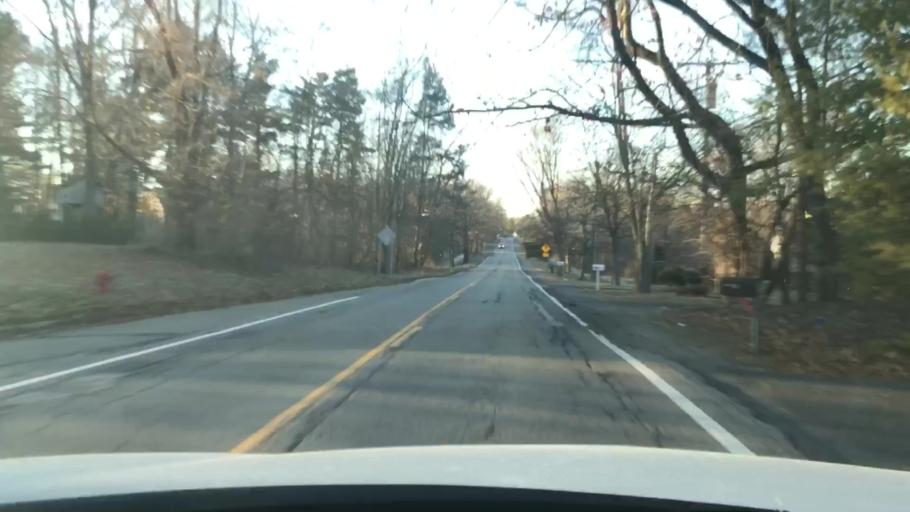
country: US
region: Michigan
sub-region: Oakland County
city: West Bloomfield Township
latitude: 42.5969
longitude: -83.4044
